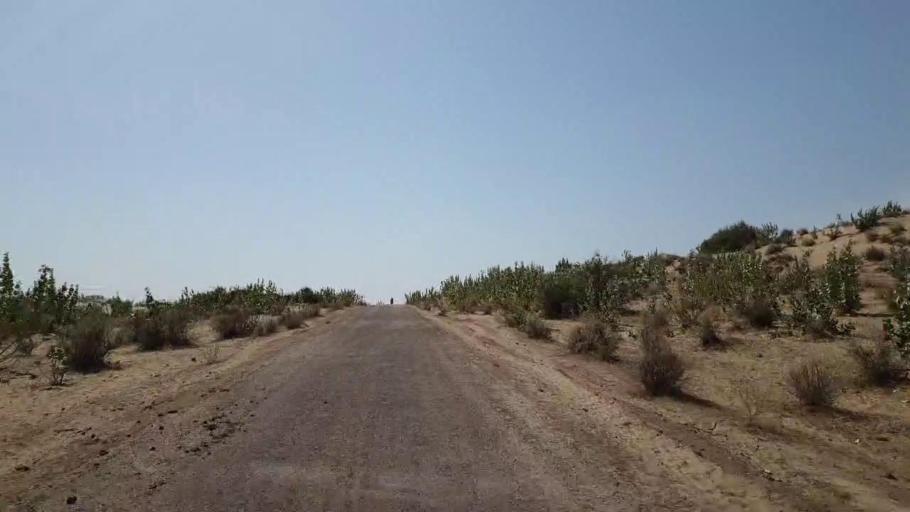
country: PK
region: Sindh
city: Umarkot
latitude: 25.2194
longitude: 69.8777
